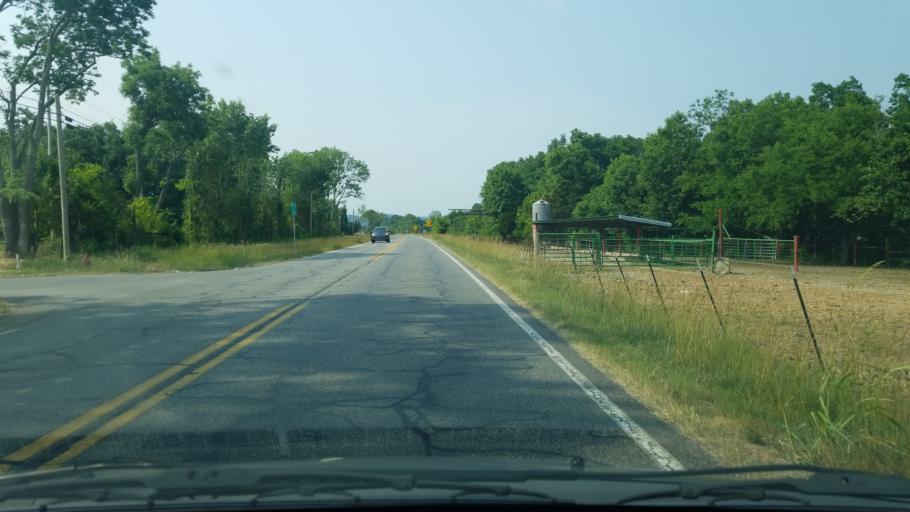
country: US
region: Georgia
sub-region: Catoosa County
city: Ringgold
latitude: 34.9603
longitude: -85.1037
